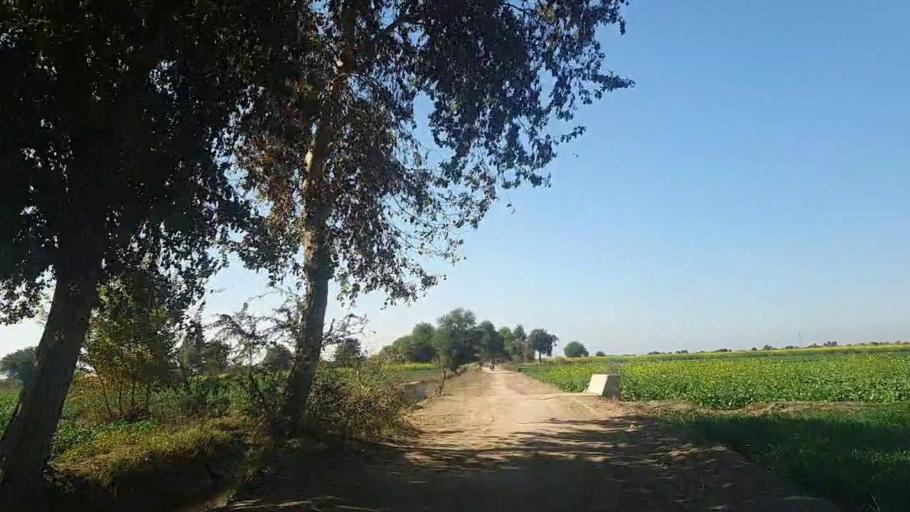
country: PK
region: Sindh
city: Khadro
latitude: 26.1571
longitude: 68.8275
